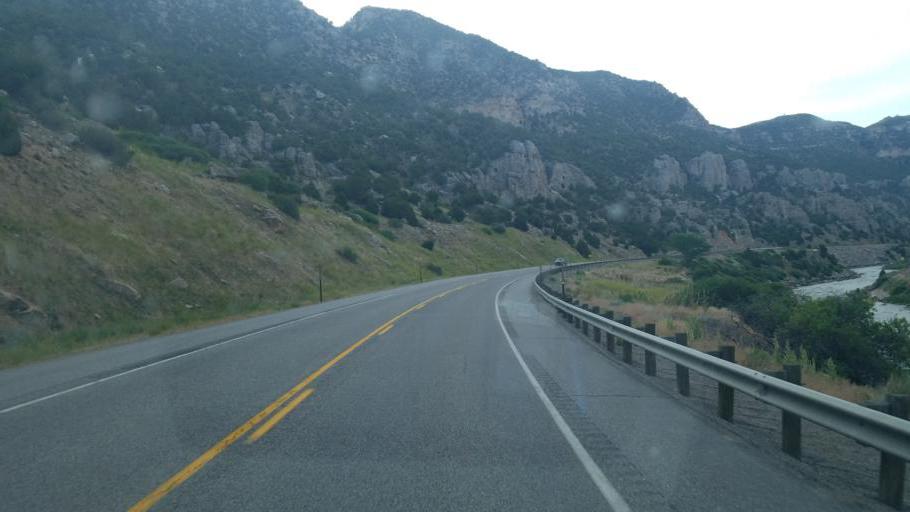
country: US
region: Wyoming
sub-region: Hot Springs County
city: Thermopolis
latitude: 43.5529
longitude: -108.1982
